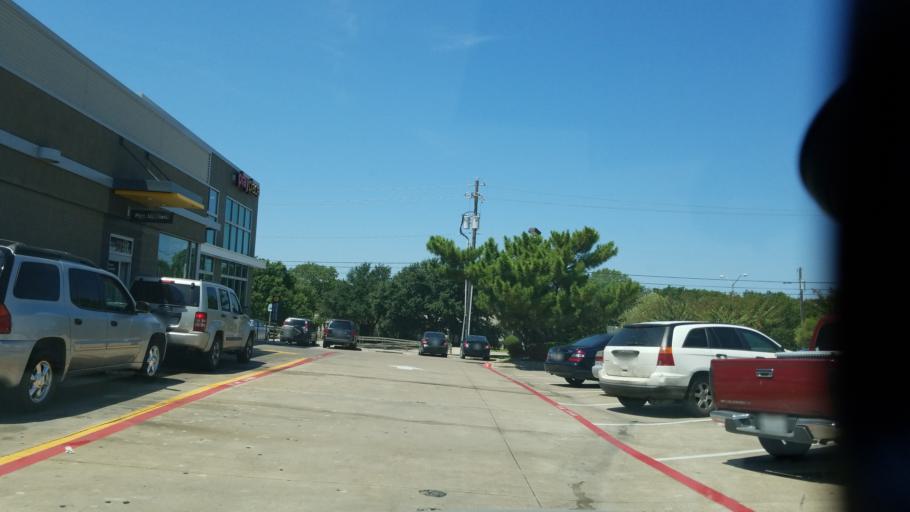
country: US
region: Texas
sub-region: Dallas County
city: Duncanville
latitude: 32.6439
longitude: -96.8907
